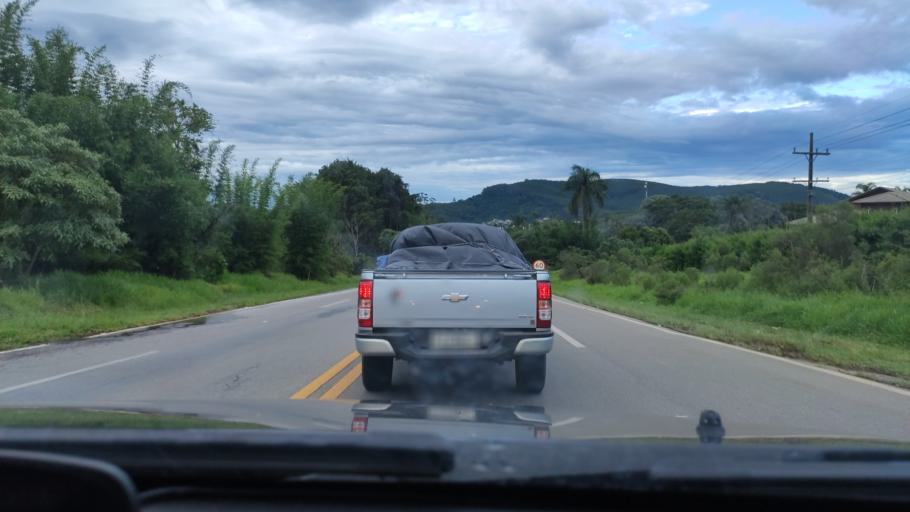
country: BR
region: Sao Paulo
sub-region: Braganca Paulista
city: Braganca Paulista
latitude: -22.8797
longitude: -46.5361
